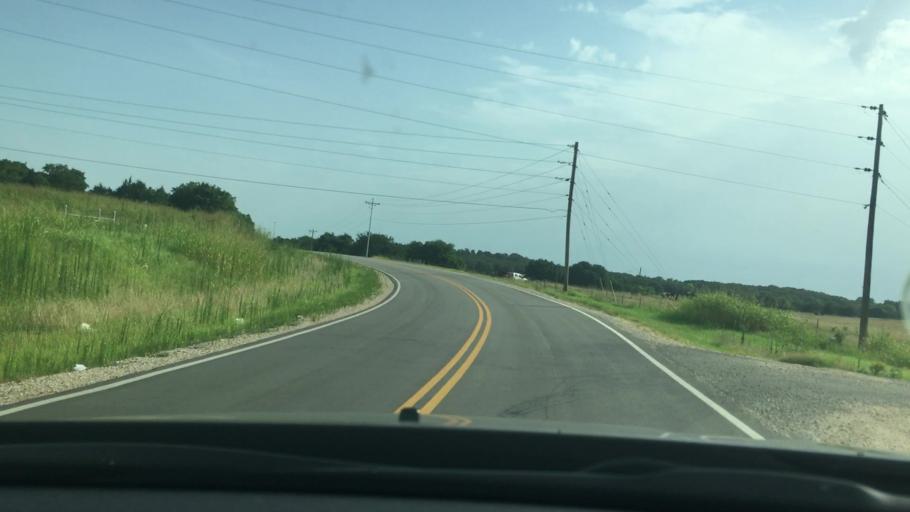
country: US
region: Oklahoma
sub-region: Pontotoc County
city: Byng
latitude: 34.8535
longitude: -96.6137
